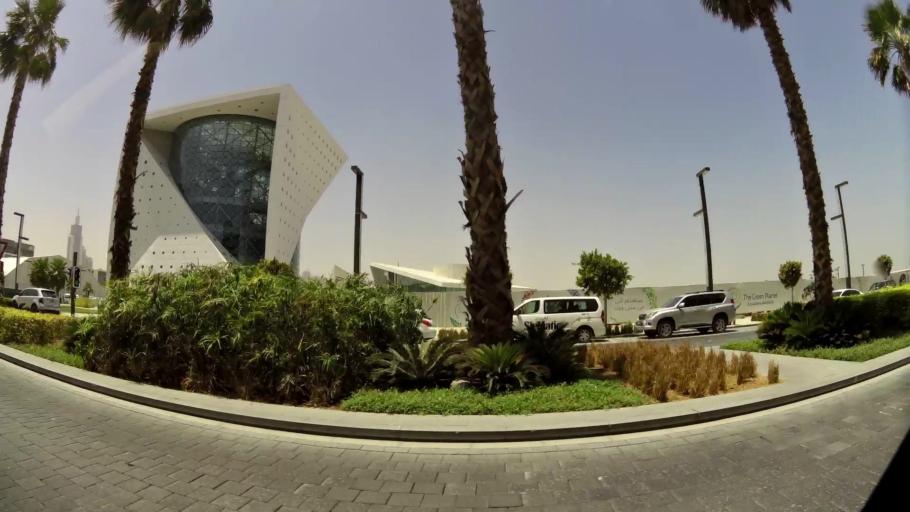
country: AE
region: Dubai
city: Dubai
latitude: 25.2069
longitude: 55.2604
